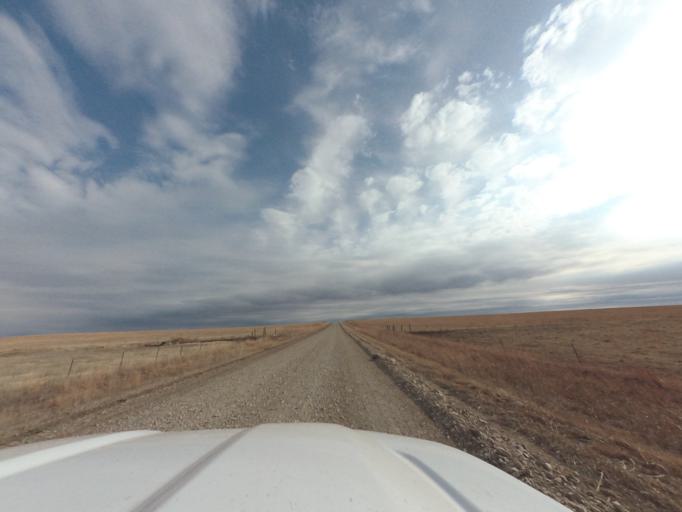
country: US
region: Kansas
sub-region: Chase County
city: Cottonwood Falls
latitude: 38.2171
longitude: -96.7049
